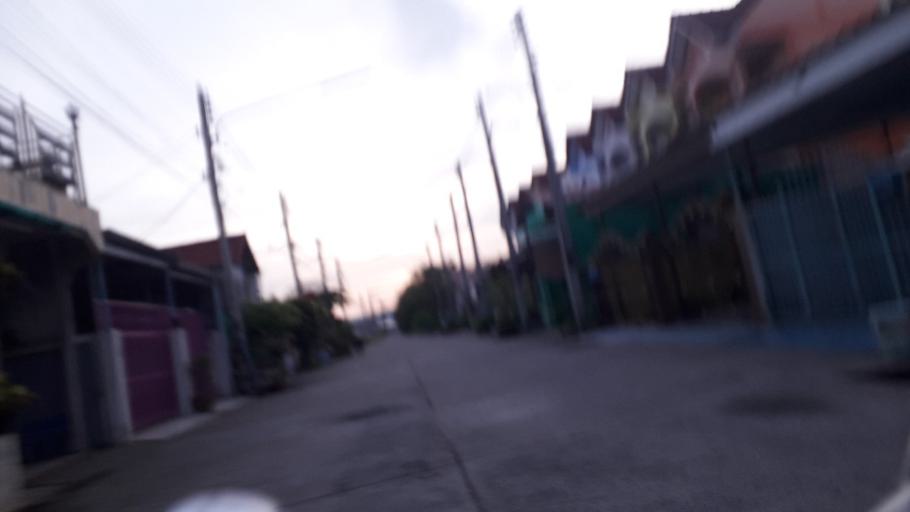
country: TH
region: Lop Buri
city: Lop Buri
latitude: 14.8300
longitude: 100.6506
